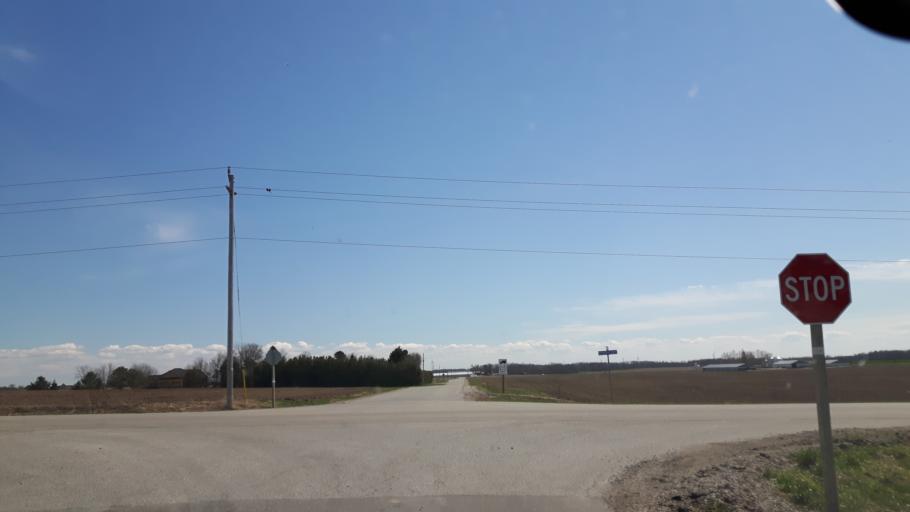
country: CA
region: Ontario
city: Bluewater
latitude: 43.5869
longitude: -81.6439
